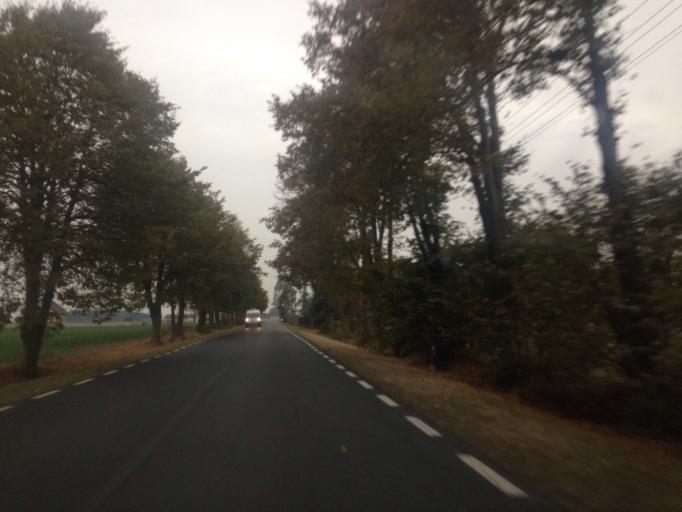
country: PL
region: Greater Poland Voivodeship
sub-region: Powiat poznanski
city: Swarzedz
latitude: 52.3513
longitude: 17.1068
